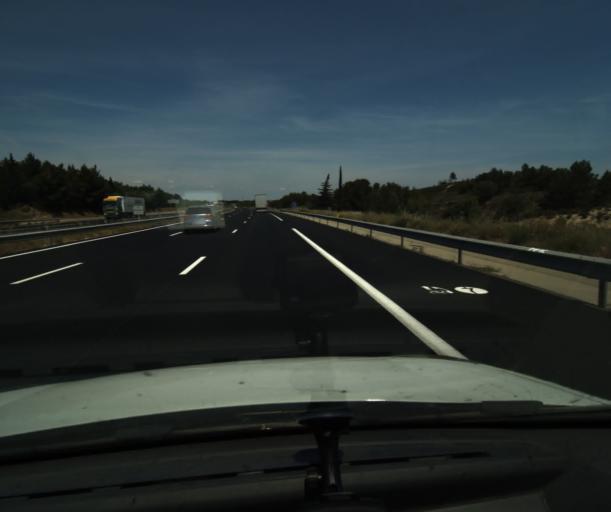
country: FR
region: Languedoc-Roussillon
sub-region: Departement de l'Aude
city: Narbonne
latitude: 43.1418
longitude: 2.9791
